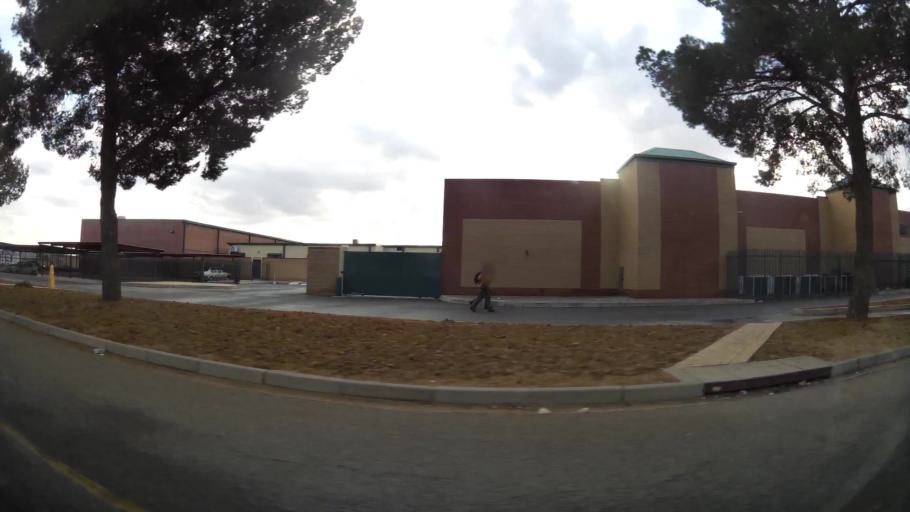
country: ZA
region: Orange Free State
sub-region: Lejweleputswa District Municipality
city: Welkom
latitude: -27.9873
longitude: 26.7348
